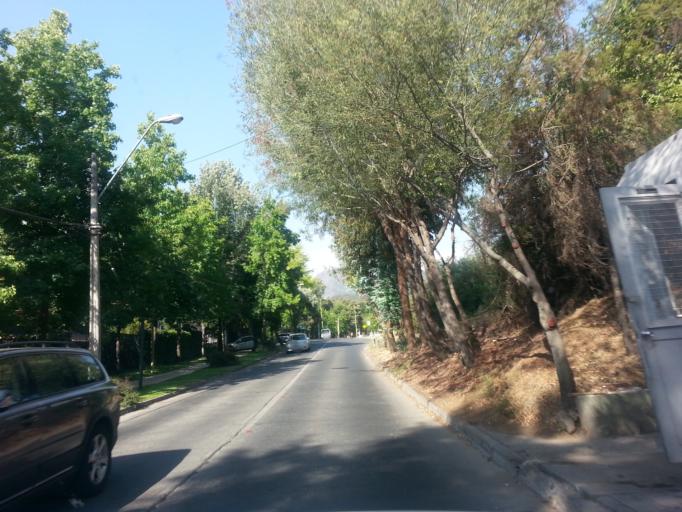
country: CL
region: Santiago Metropolitan
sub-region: Provincia de Santiago
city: Villa Presidente Frei, Nunoa, Santiago, Chile
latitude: -33.3793
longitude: -70.5079
